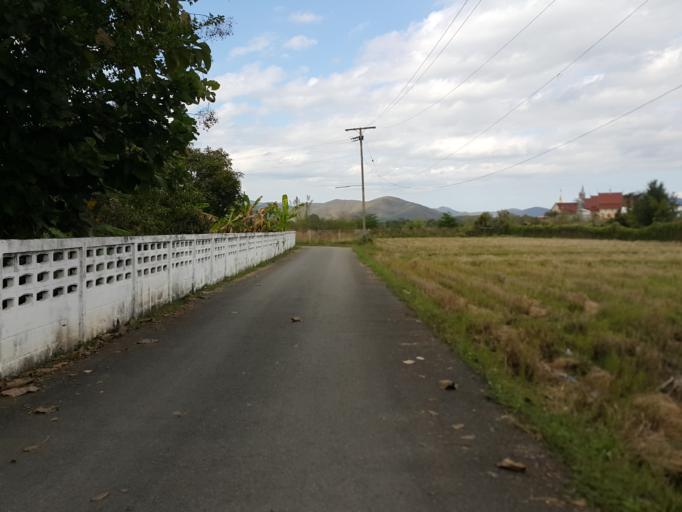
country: TH
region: Chiang Mai
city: San Sai
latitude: 18.8667
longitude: 99.1089
